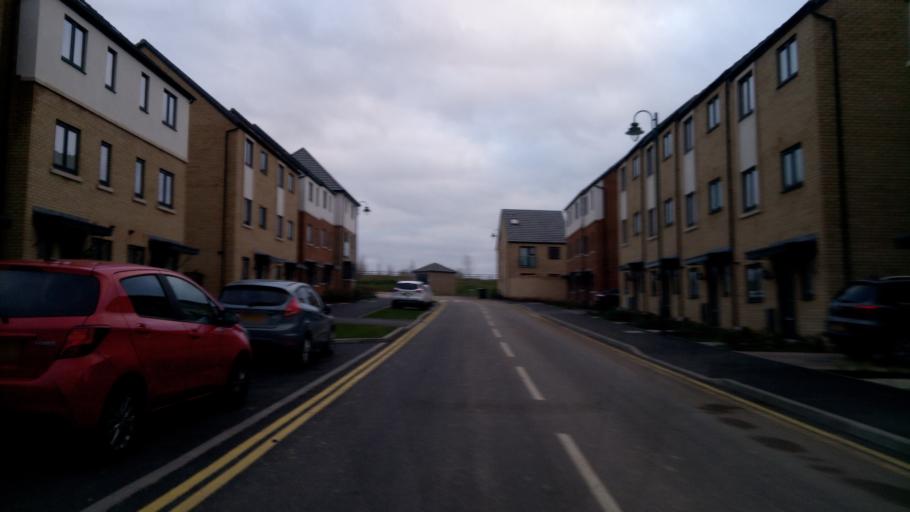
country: GB
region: England
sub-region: Cambridgeshire
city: Yaxley
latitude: 52.5281
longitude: -0.2853
